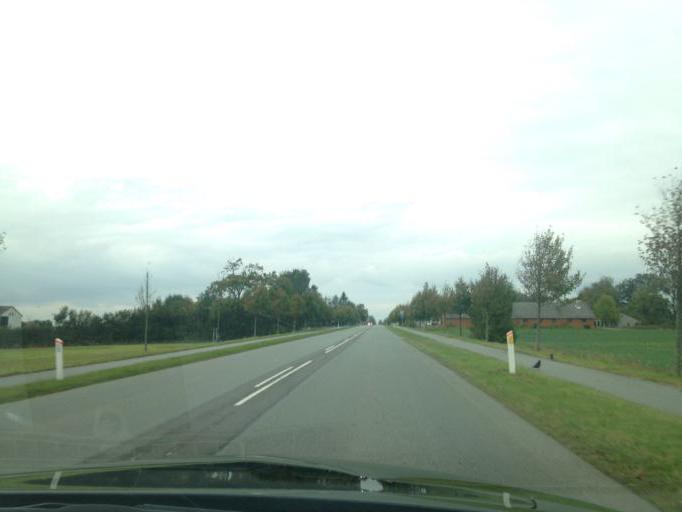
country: DK
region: South Denmark
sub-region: Kolding Kommune
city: Christiansfeld
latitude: 55.3720
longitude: 9.4817
